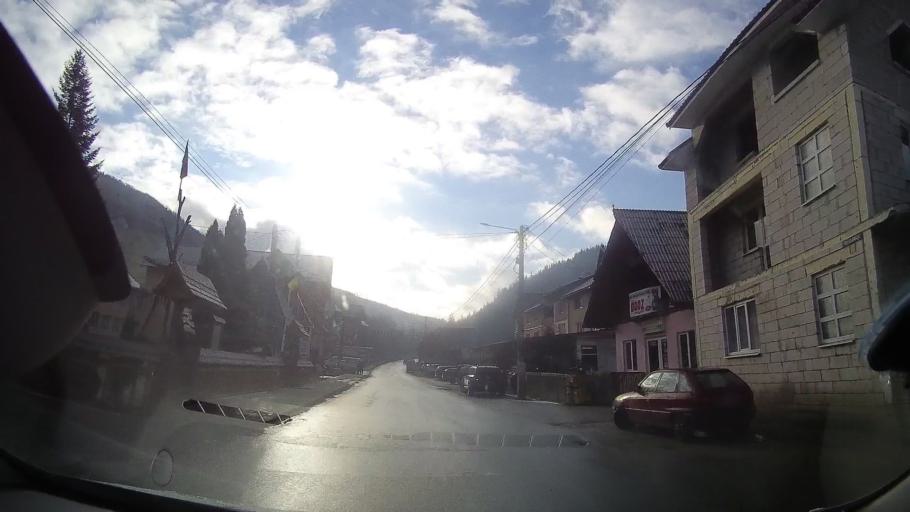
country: RO
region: Alba
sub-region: Comuna Albac
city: Albac
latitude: 46.4480
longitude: 22.9640
